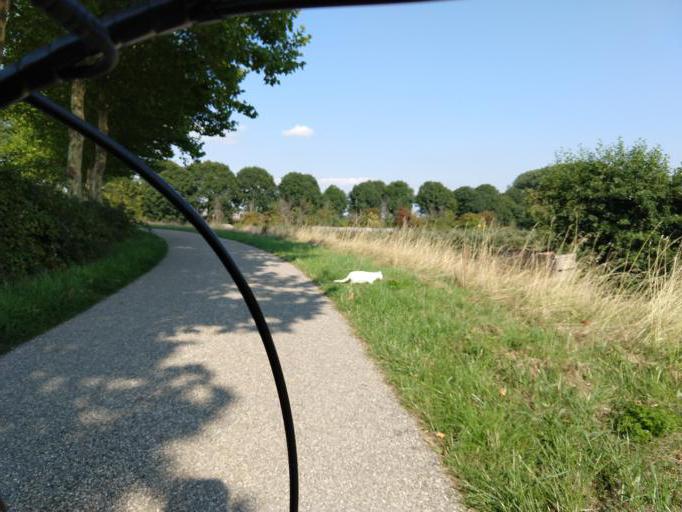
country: NL
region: Zeeland
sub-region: Gemeente Terneuzen
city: Terneuzen
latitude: 51.4161
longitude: 3.8451
